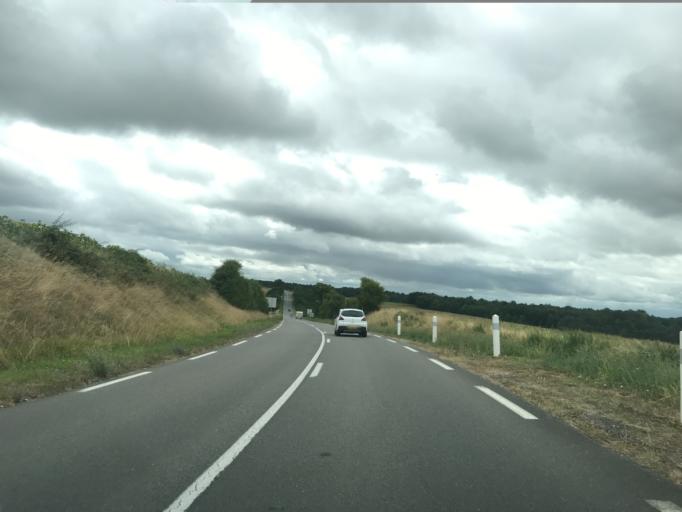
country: FR
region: Poitou-Charentes
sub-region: Departement de la Charente
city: Dignac
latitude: 45.5045
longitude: 0.3283
